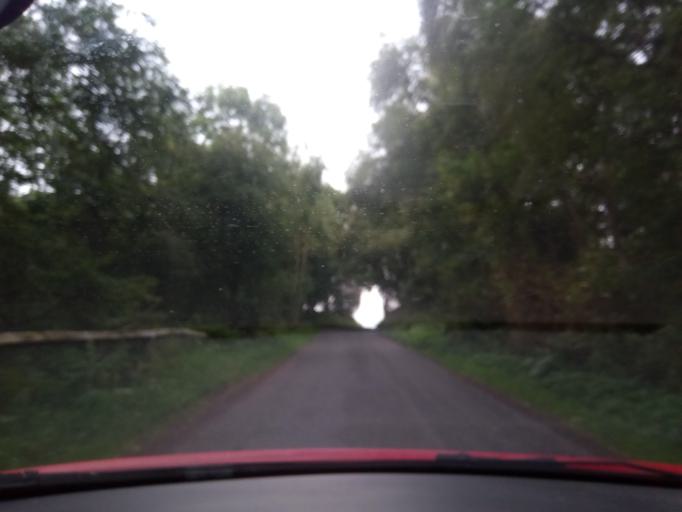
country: GB
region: England
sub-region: Northumberland
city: Otterburn
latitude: 55.3170
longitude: -2.0703
